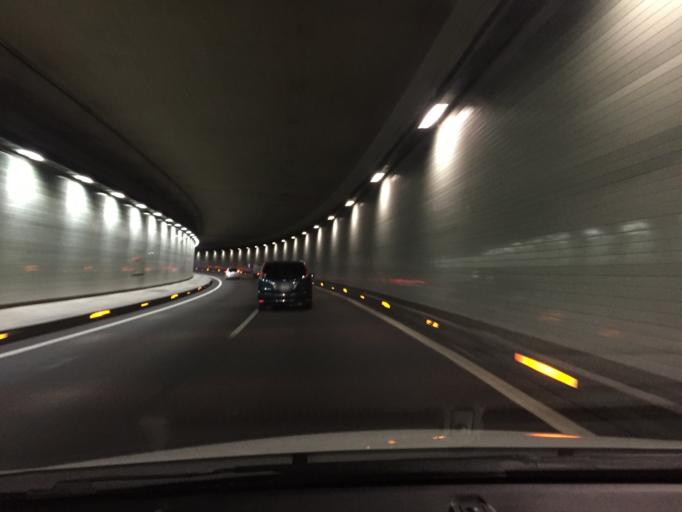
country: JP
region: Tokyo
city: Fussa
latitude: 35.7919
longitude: 139.3020
